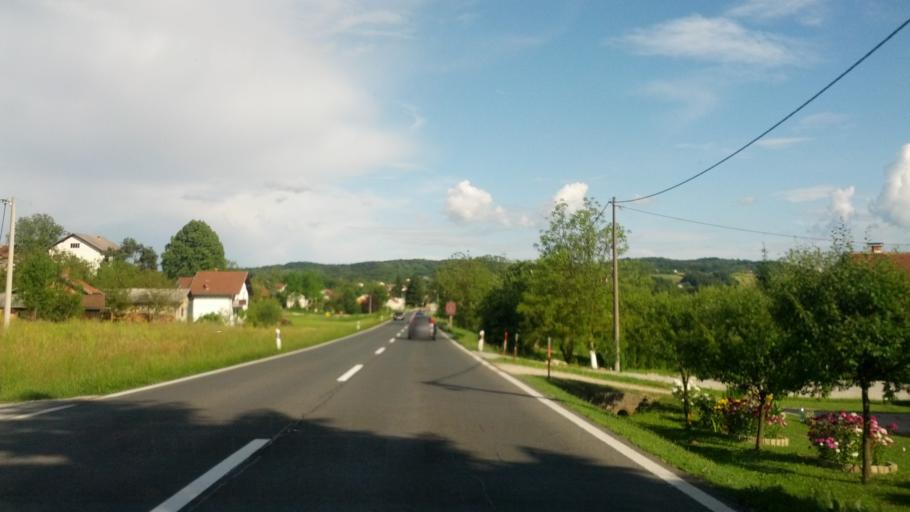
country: HR
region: Karlovacka
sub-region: Grad Karlovac
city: Karlovac
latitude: 45.4330
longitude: 15.5970
